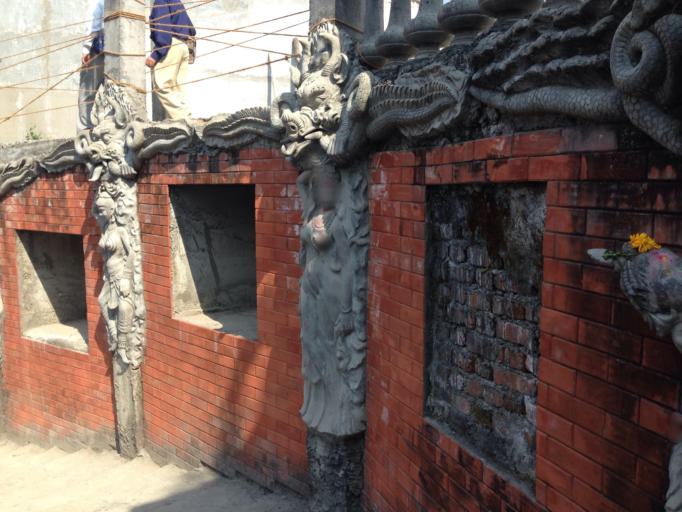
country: NP
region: Western Region
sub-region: Gandaki Zone
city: Pokhara
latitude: 28.1893
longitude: 83.9578
